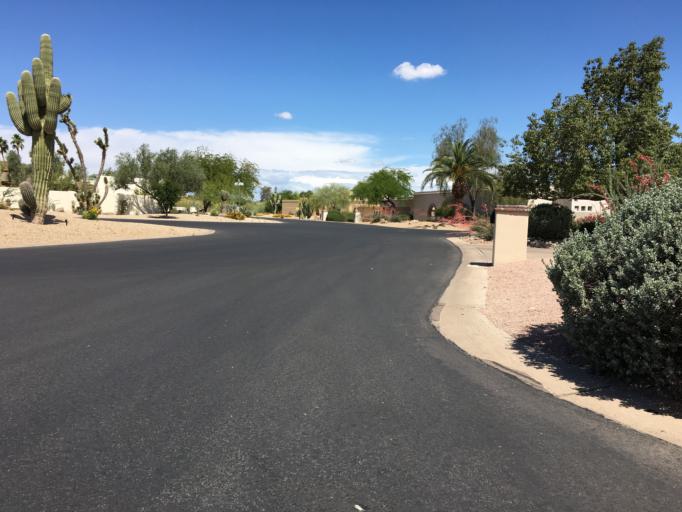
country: US
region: Arizona
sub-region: Maricopa County
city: Paradise Valley
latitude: 33.5752
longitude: -111.9890
